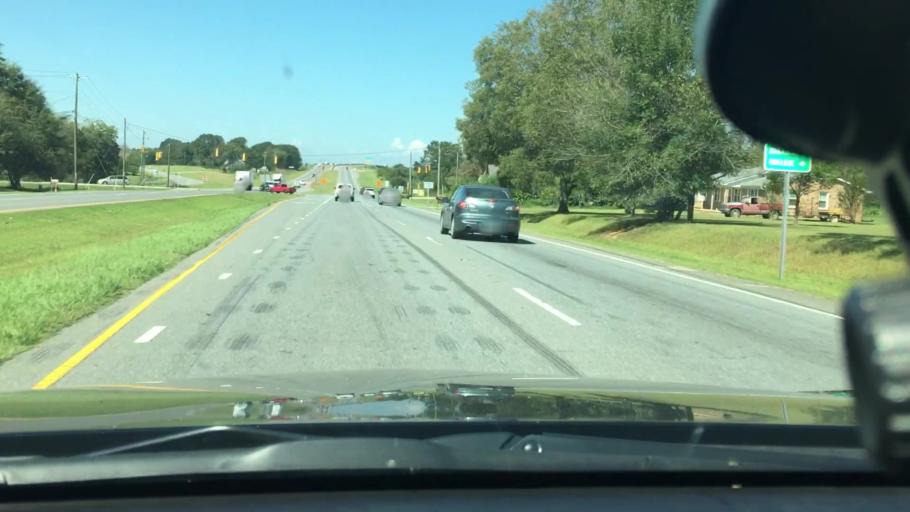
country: US
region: North Carolina
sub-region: Cleveland County
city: Boiling Springs
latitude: 35.2926
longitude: -81.6442
